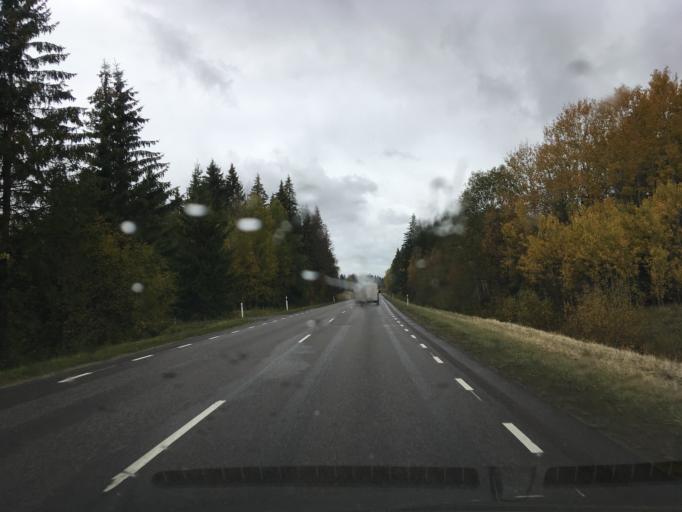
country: EE
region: Harju
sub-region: Anija vald
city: Kehra
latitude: 59.3344
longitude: 25.3124
